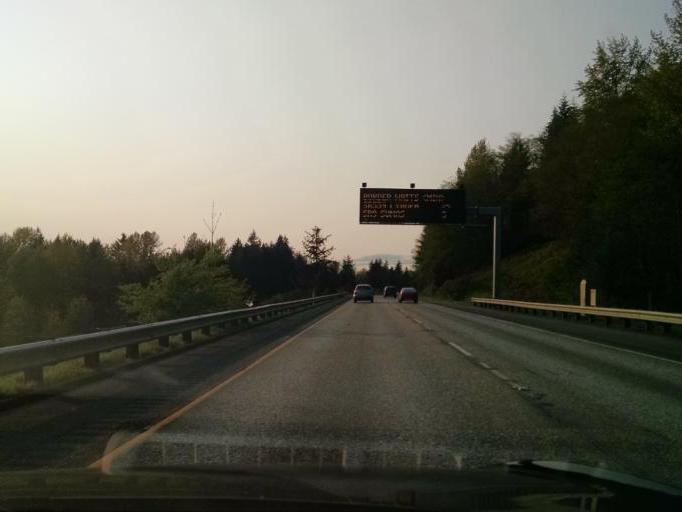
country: US
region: Washington
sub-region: Whatcom County
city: Bellingham
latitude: 48.7027
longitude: -122.4729
